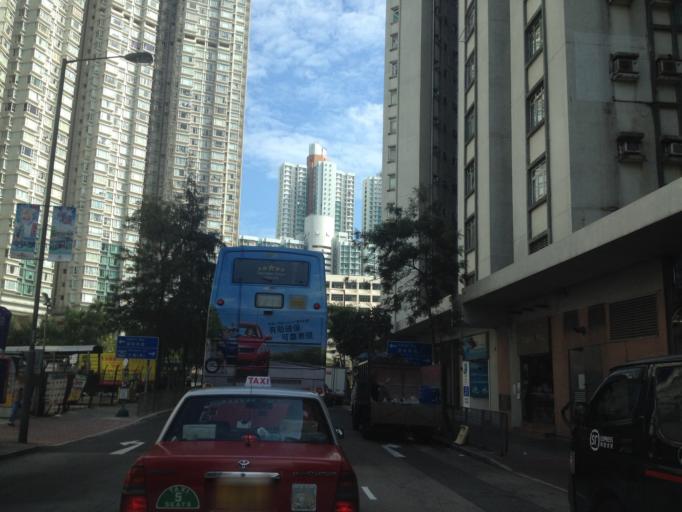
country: HK
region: Wanchai
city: Wan Chai
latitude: 22.2843
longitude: 114.2233
